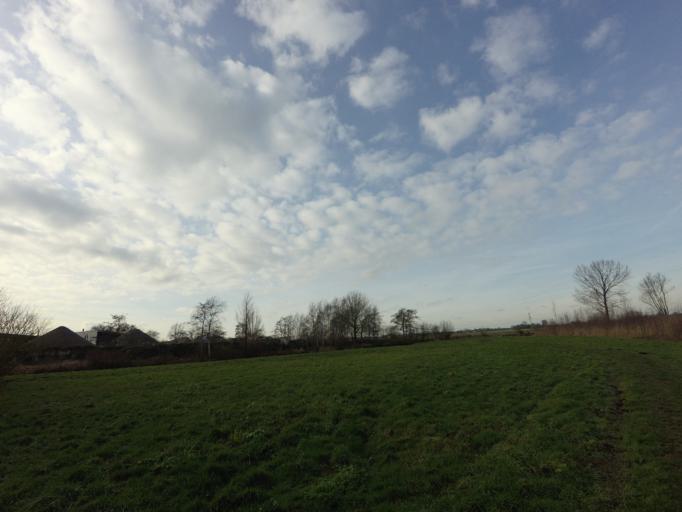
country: NL
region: Utrecht
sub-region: Gemeente Oudewater
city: Oudewater
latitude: 52.0387
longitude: 4.8683
